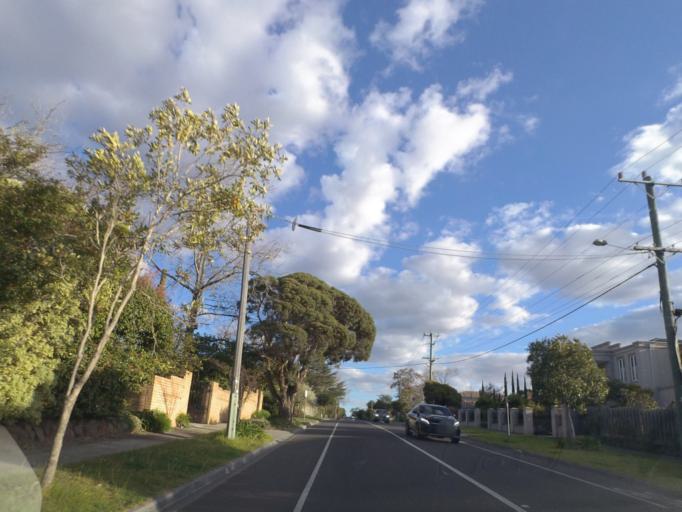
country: AU
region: Victoria
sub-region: Boroondara
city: Balwyn North
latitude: -37.7933
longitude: 145.0992
